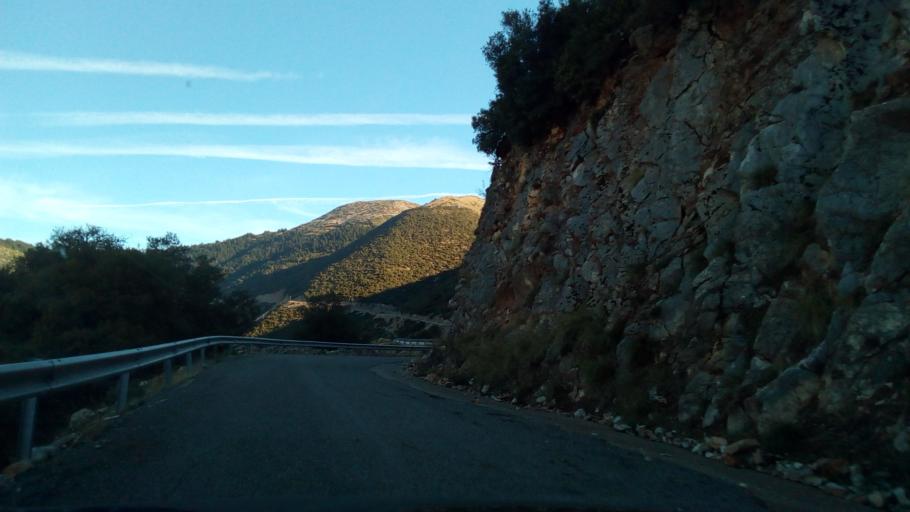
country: GR
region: West Greece
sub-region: Nomos Aitolias kai Akarnanias
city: Nafpaktos
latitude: 38.5102
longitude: 21.8426
